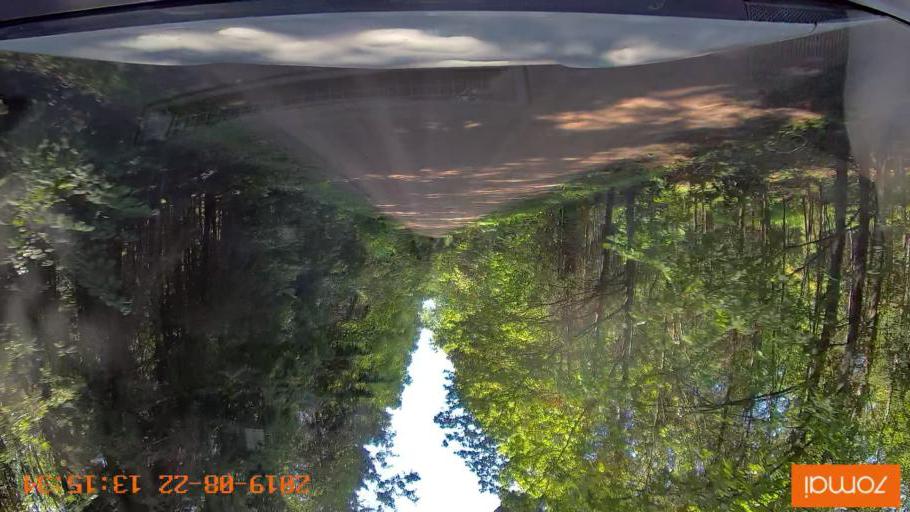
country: BY
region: Minsk
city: Prawdzinski
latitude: 53.2594
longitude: 27.8984
